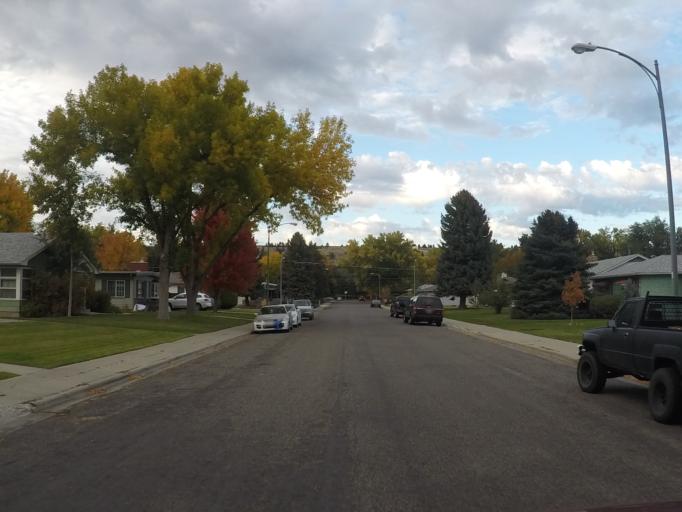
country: US
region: Montana
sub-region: Yellowstone County
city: Billings
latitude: 45.7905
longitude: -108.5512
